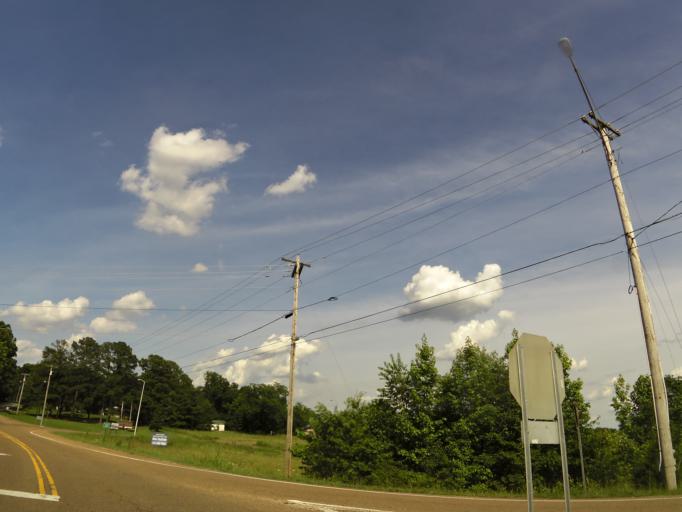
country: US
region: Tennessee
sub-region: Carroll County
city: Huntingdon
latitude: 36.0151
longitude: -88.3948
